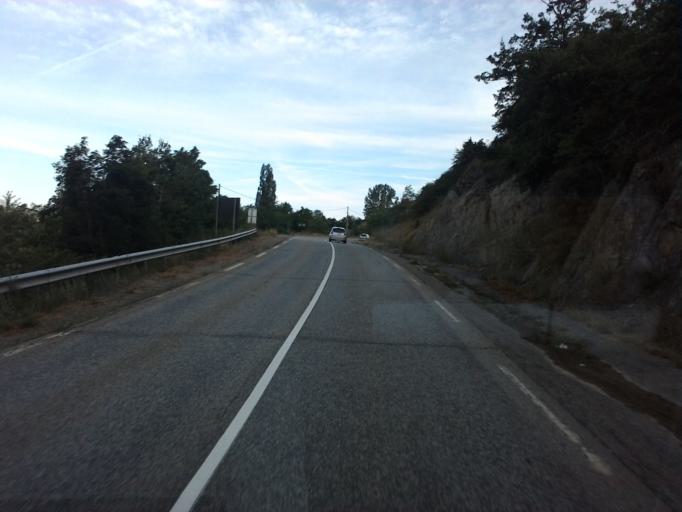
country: FR
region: Rhone-Alpes
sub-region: Departement de l'Isere
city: La Mure
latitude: 44.8641
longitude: 5.8541
